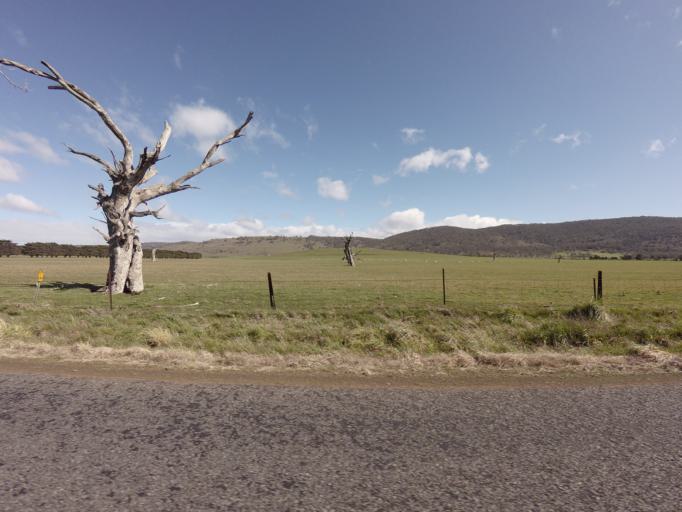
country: AU
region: Tasmania
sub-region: Northern Midlands
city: Evandale
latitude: -41.9917
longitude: 147.4529
